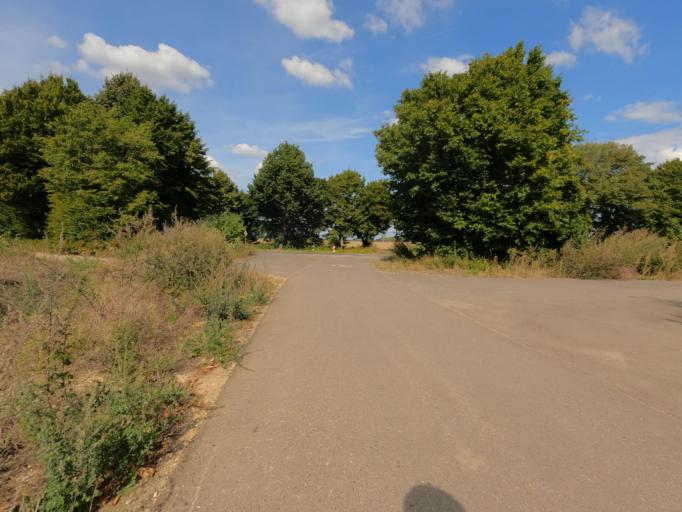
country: DE
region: North Rhine-Westphalia
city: Erkelenz
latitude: 51.0866
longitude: 6.2928
